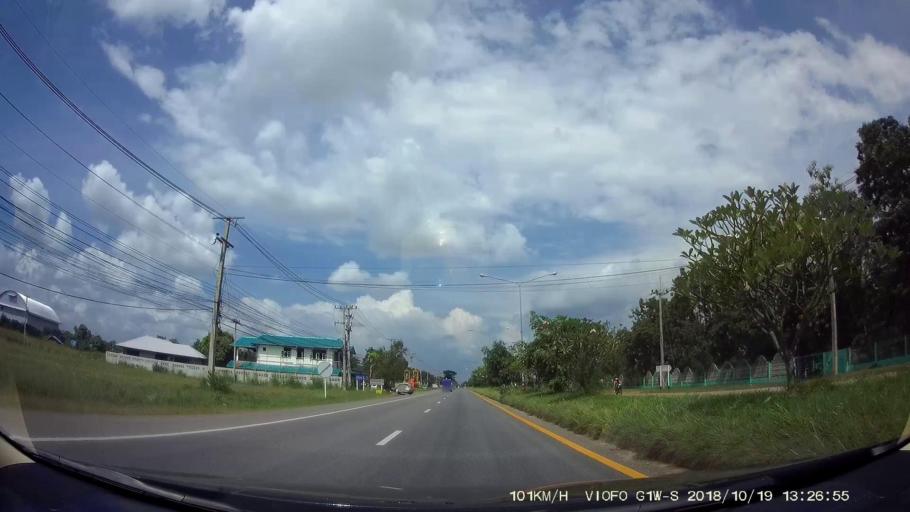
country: TH
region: Chaiyaphum
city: Chatturat
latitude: 15.5411
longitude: 101.8369
